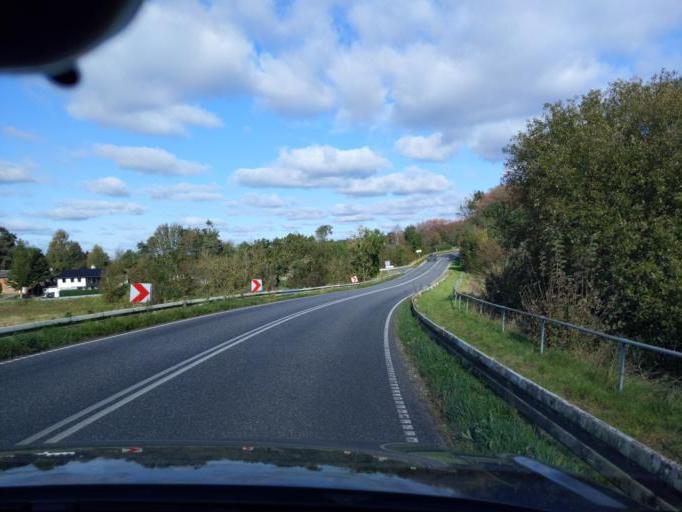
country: DK
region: Central Jutland
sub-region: Viborg Kommune
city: Bjerringbro
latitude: 56.5009
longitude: 9.5845
